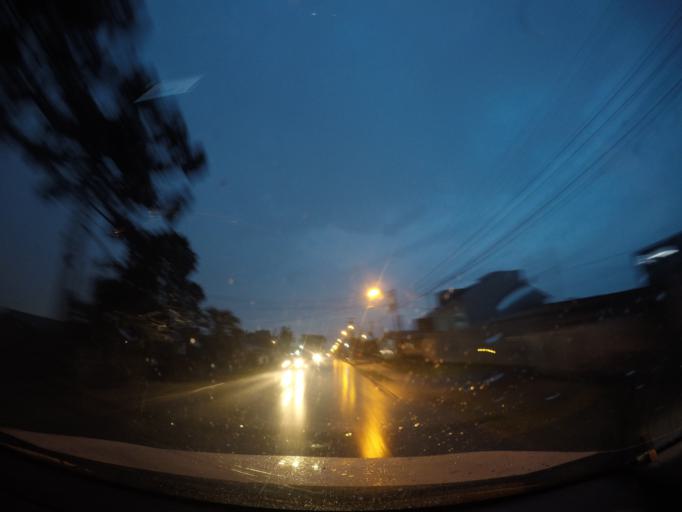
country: BR
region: Parana
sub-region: Sao Jose Dos Pinhais
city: Sao Jose dos Pinhais
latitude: -25.5026
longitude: -49.2330
